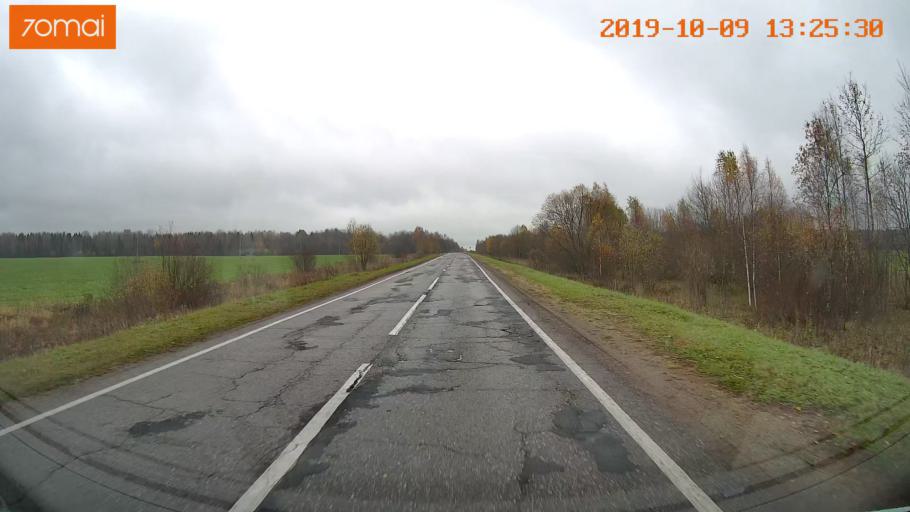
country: RU
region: Jaroslavl
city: Lyubim
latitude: 58.3279
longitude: 40.9116
